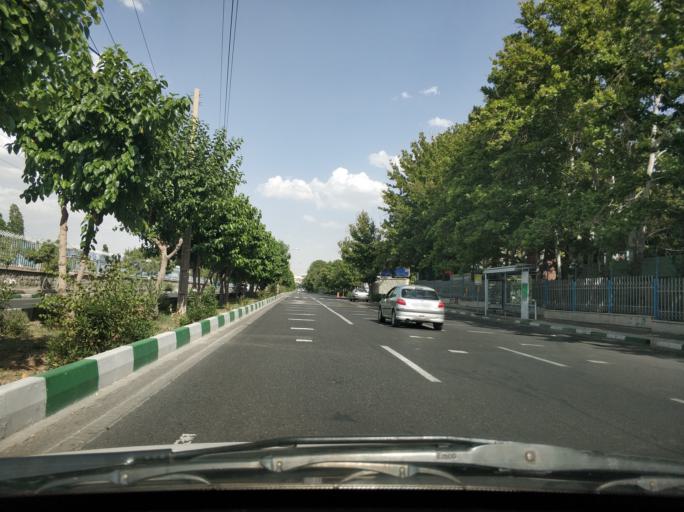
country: IR
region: Tehran
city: Tajrish
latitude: 35.7444
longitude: 51.5780
